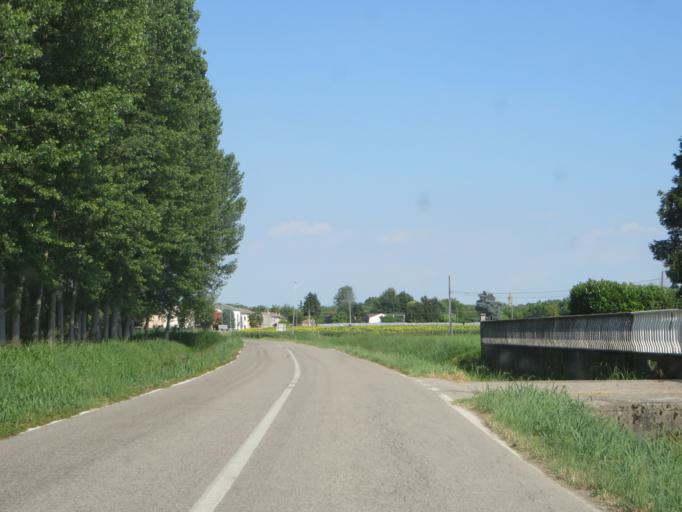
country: IT
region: Veneto
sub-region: Provincia di Verona
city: Angiari
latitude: 45.2246
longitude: 11.2658
